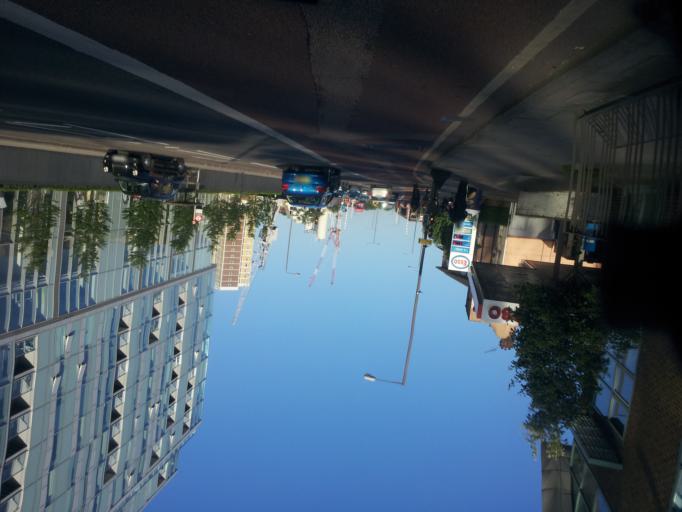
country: GB
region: England
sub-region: Greater London
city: Poplar
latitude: 51.4812
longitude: -0.0189
